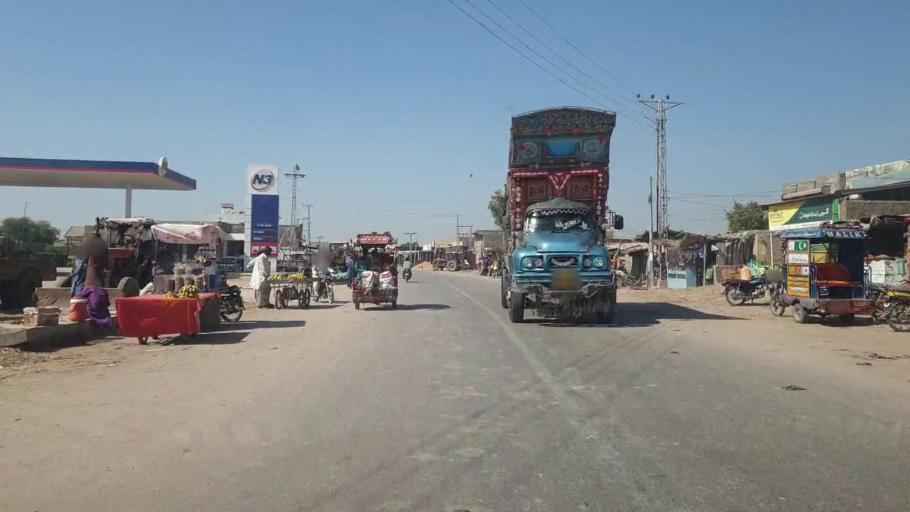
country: PK
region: Sindh
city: Talhar
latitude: 24.8855
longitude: 68.8079
